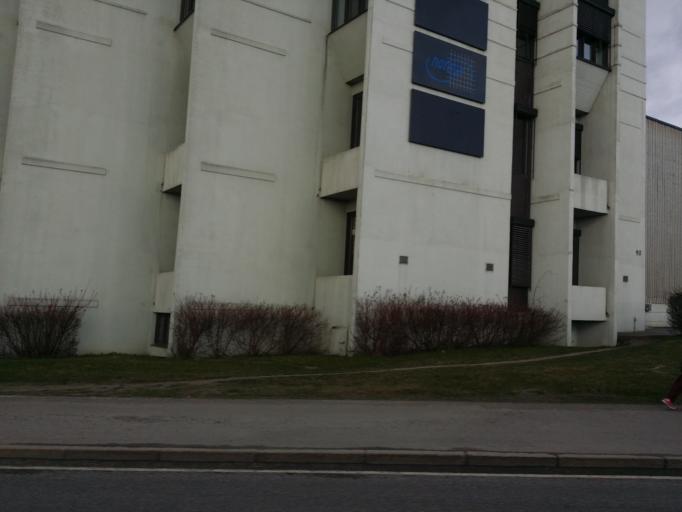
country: NO
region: Oslo
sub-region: Oslo
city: Oslo
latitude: 59.9251
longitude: 10.8126
